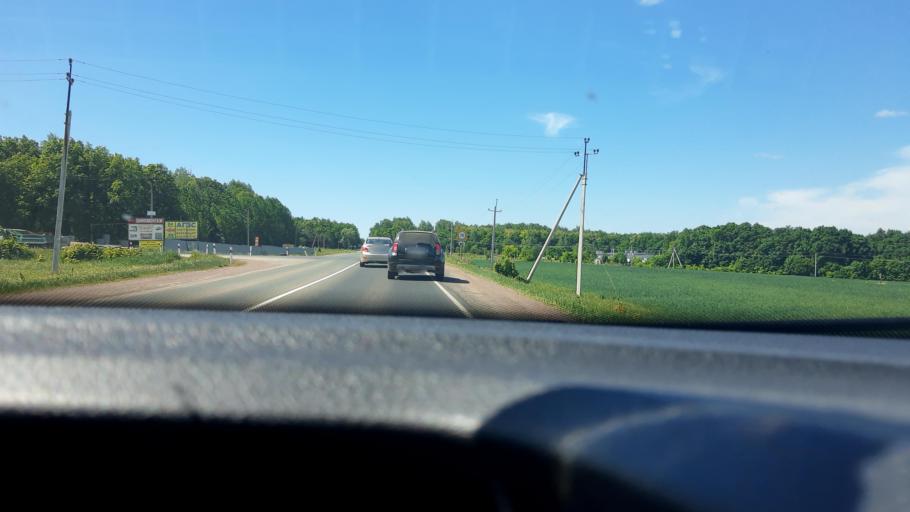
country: RU
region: Bashkortostan
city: Avdon
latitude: 54.5770
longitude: 55.7226
